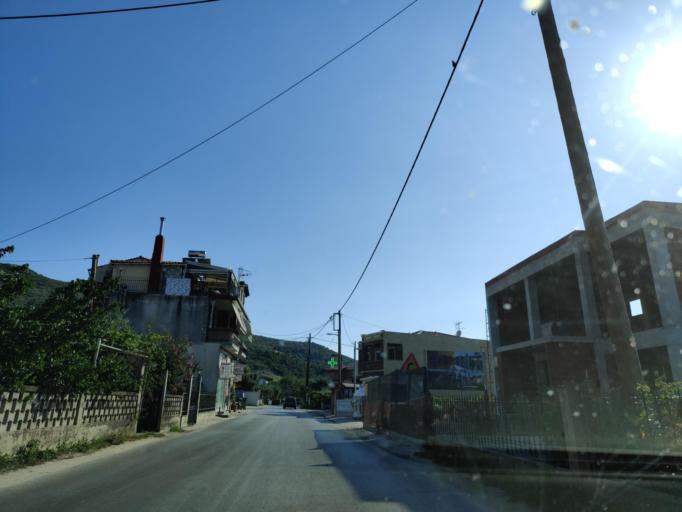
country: GR
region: East Macedonia and Thrace
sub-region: Nomos Kavalas
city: Prinos
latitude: 40.7405
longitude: 24.5750
